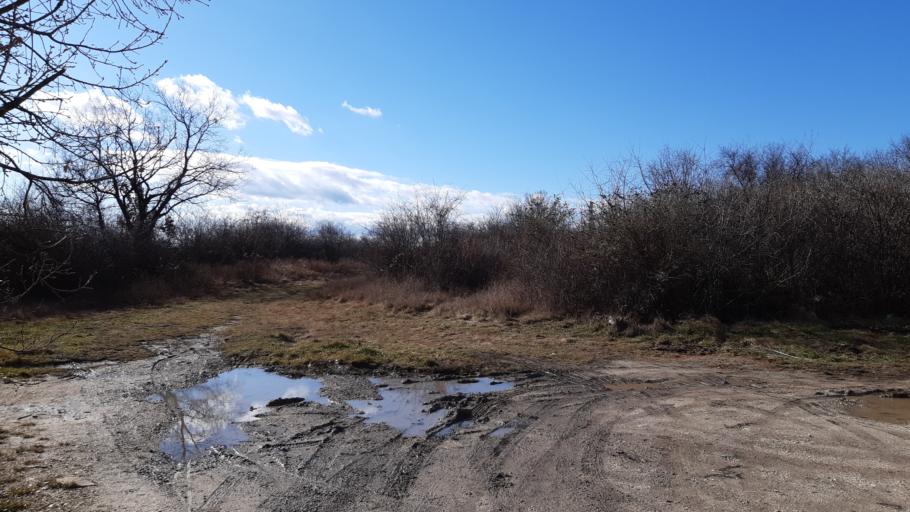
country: HU
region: Pest
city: Diosd
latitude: 47.4302
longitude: 18.9760
